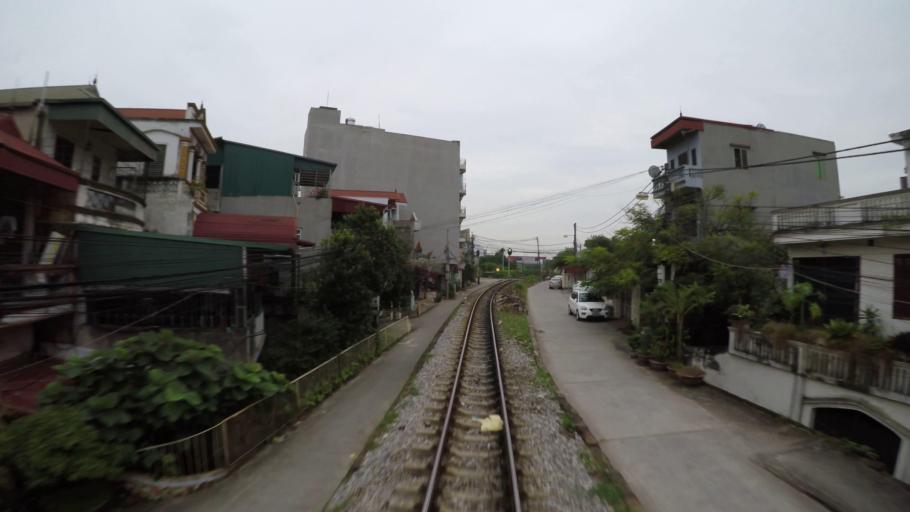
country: VN
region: Ha Noi
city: Trau Quy
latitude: 21.0204
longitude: 105.9390
